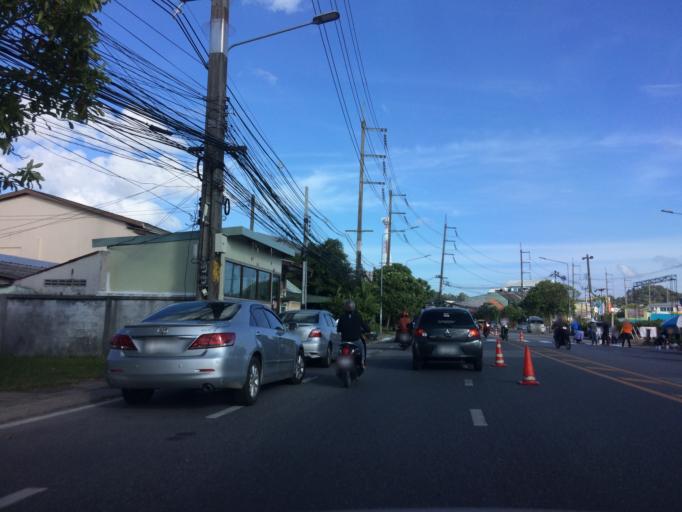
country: TH
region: Phuket
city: Kathu
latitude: 7.9045
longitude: 98.3516
